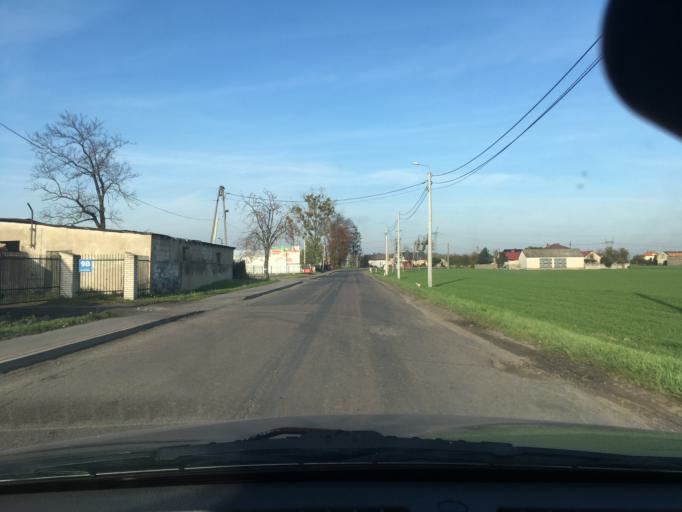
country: PL
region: Masovian Voivodeship
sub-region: Powiat plocki
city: Mala Wies
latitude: 52.4614
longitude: 20.1087
